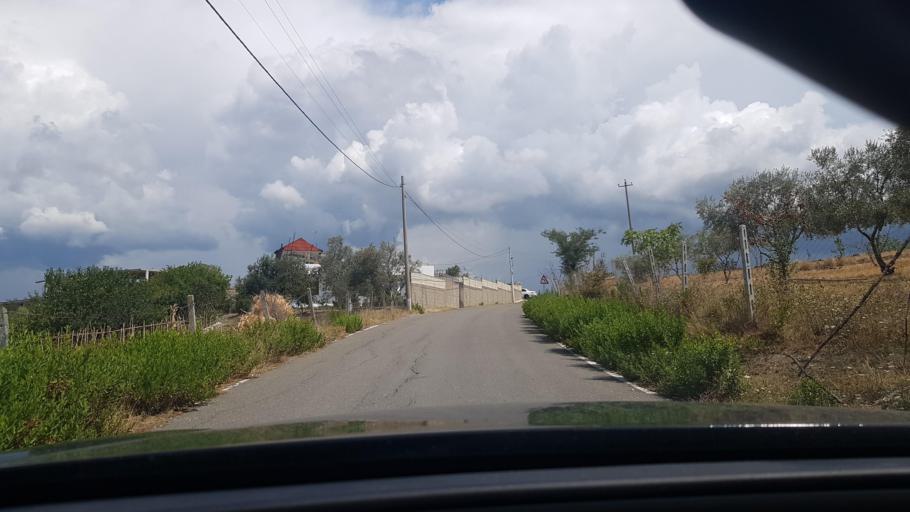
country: AL
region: Durres
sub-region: Rrethi i Durresit
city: Rrashbull
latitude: 41.2918
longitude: 19.5368
